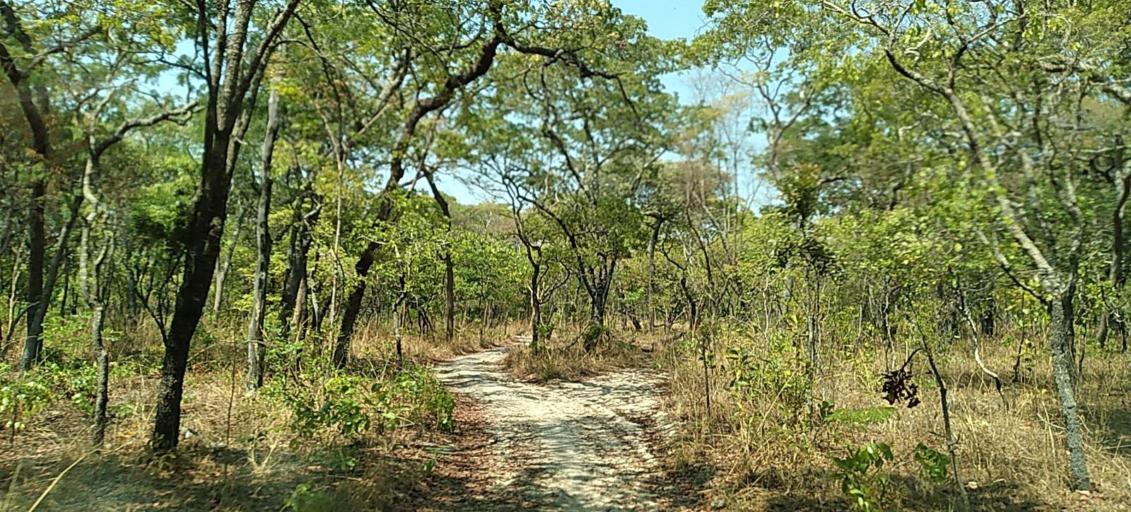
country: ZM
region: Copperbelt
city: Mpongwe
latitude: -13.7966
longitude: 28.0833
